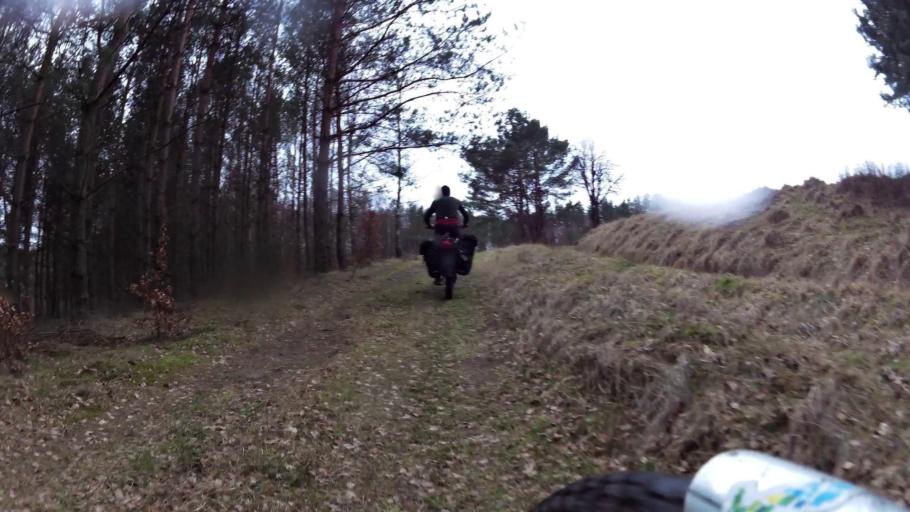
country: PL
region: Pomeranian Voivodeship
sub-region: Powiat bytowski
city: Trzebielino
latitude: 54.0779
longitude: 17.1176
